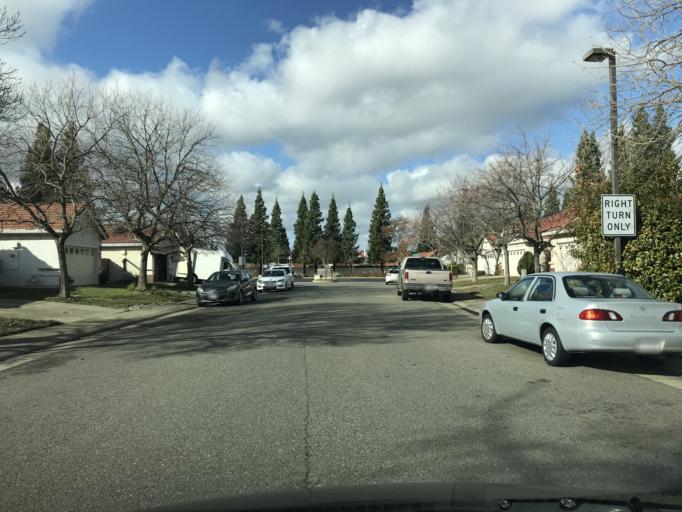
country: US
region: California
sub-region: Sacramento County
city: Folsom
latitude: 38.6621
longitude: -121.1371
